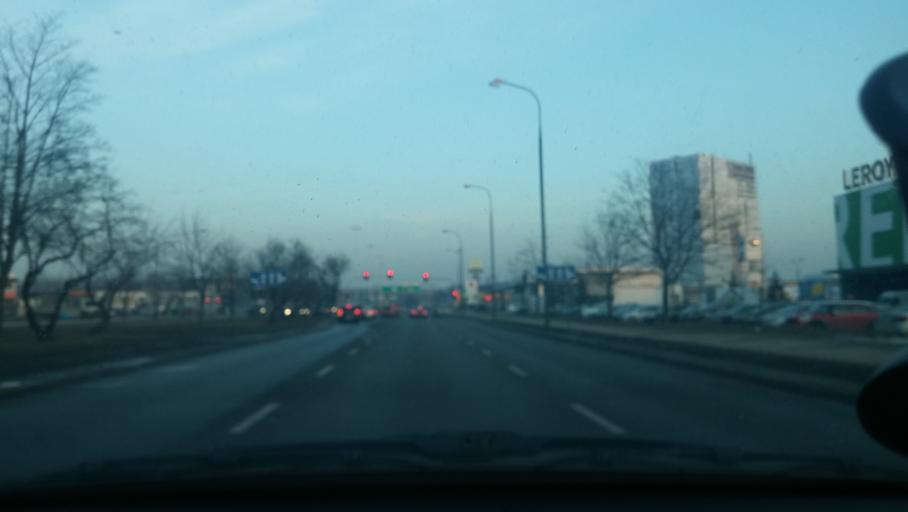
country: PL
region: Masovian Voivodeship
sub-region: Warszawa
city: Praga Poludnie
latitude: 52.2332
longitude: 21.1109
